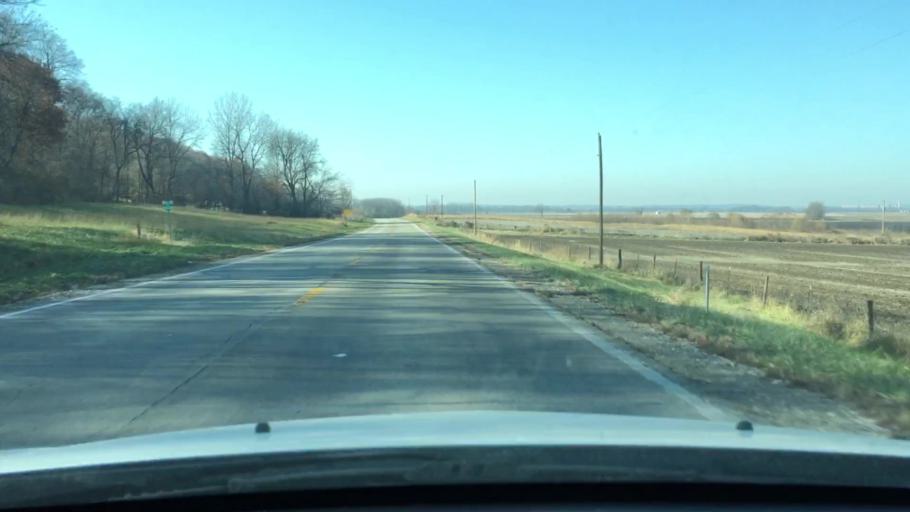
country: US
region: Illinois
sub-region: Morgan County
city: Meredosia
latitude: 39.7426
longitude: -90.5474
